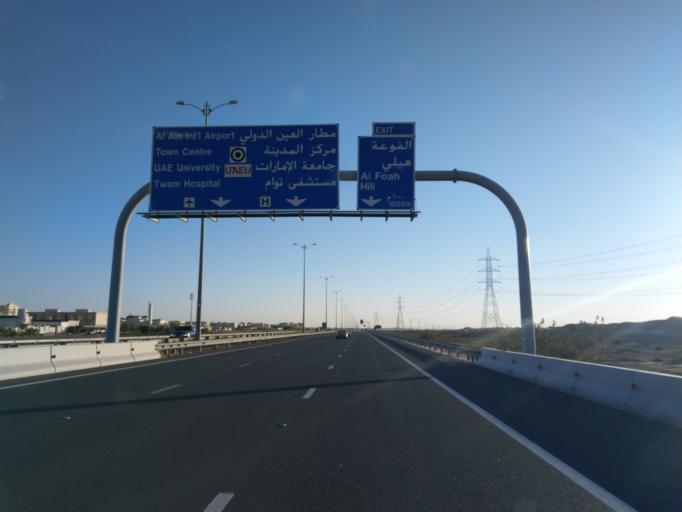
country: OM
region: Al Buraimi
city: Al Buraymi
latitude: 24.3582
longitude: 55.7860
